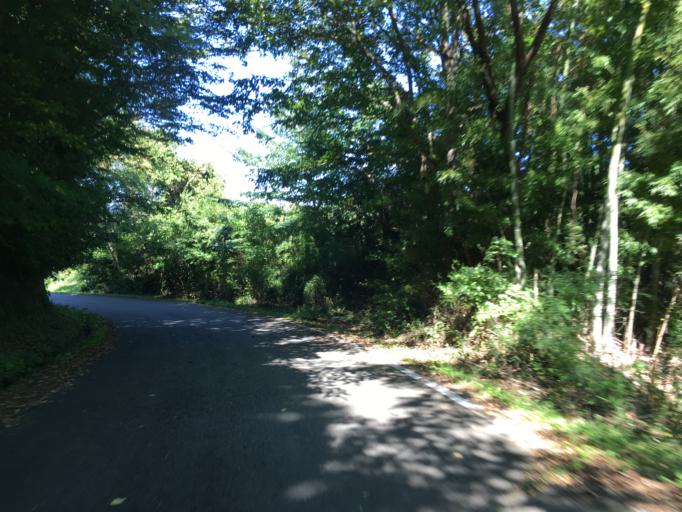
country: JP
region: Fukushima
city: Ishikawa
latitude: 37.2699
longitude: 140.5487
